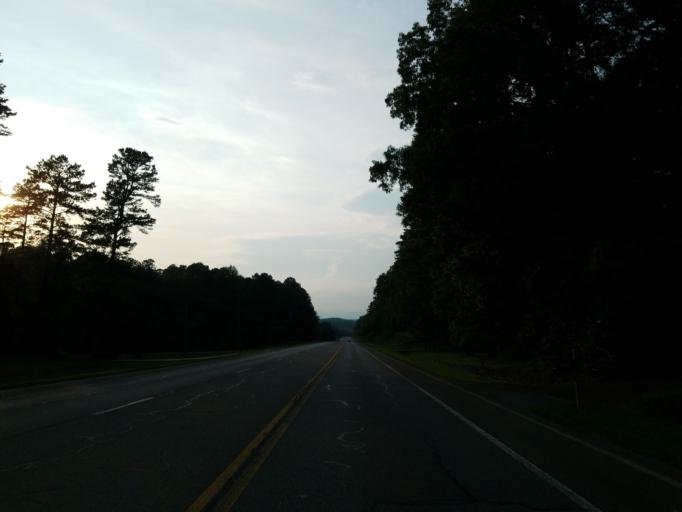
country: US
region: Georgia
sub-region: Gilmer County
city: Ellijay
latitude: 34.6607
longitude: -84.4466
